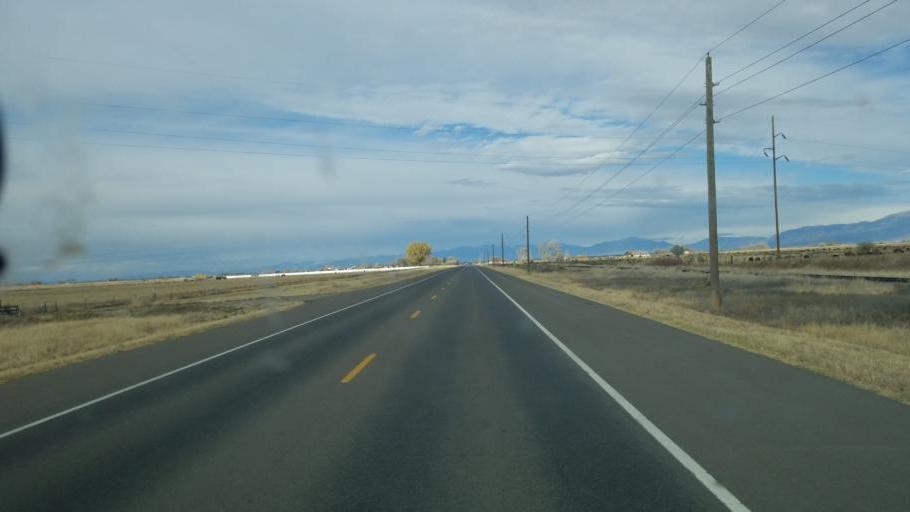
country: US
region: Colorado
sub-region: Alamosa County
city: Alamosa
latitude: 37.3849
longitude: -105.9146
